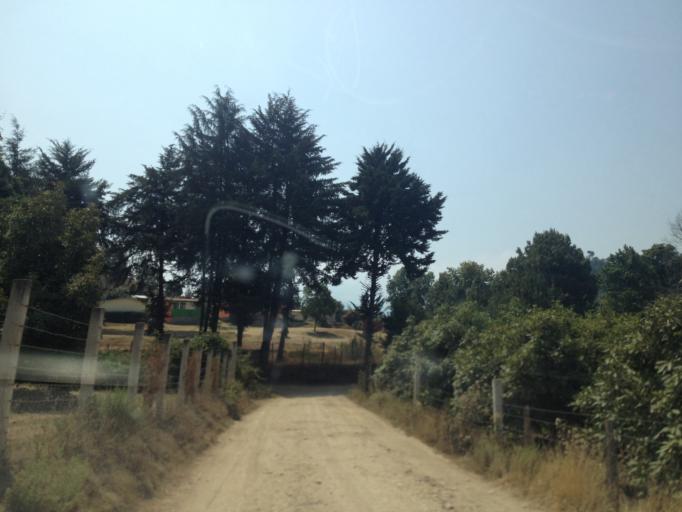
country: MX
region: Michoacan
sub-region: Zitacuaro
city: Macutzio
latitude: 19.4947
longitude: -100.3253
